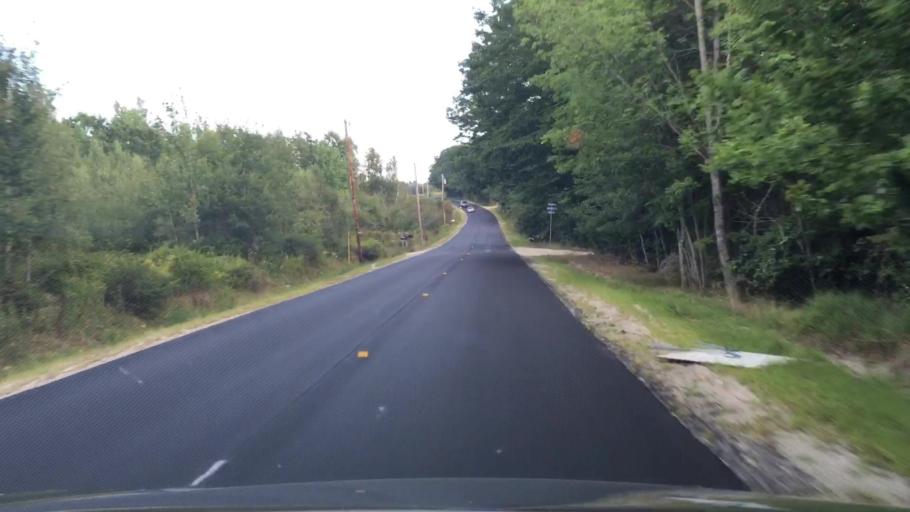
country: US
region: Maine
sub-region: Hancock County
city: Penobscot
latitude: 44.5399
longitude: -68.6159
